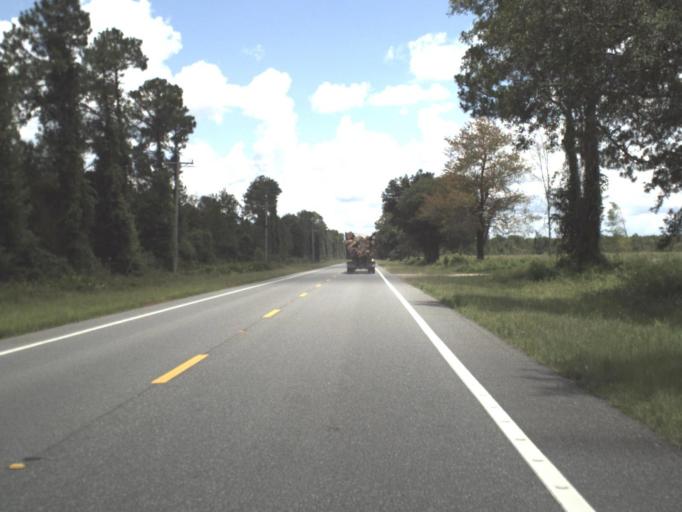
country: US
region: Florida
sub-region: Taylor County
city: Perry
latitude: 30.1427
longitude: -83.8023
